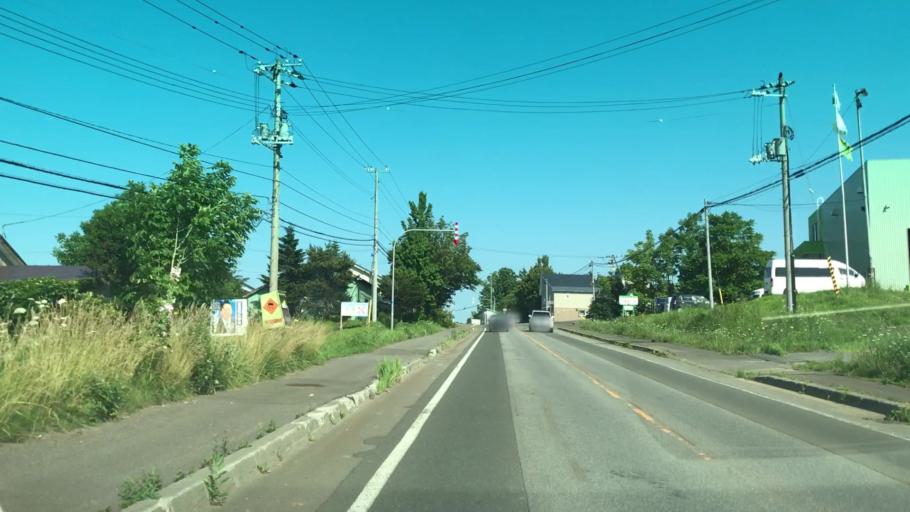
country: JP
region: Hokkaido
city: Iwanai
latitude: 42.9799
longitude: 140.5800
